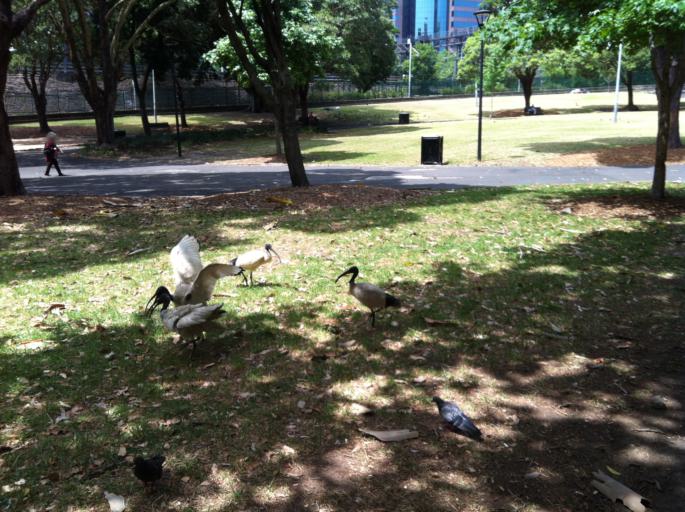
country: AU
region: New South Wales
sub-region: City of Sydney
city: Haymarket
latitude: -33.8813
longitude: 151.2077
